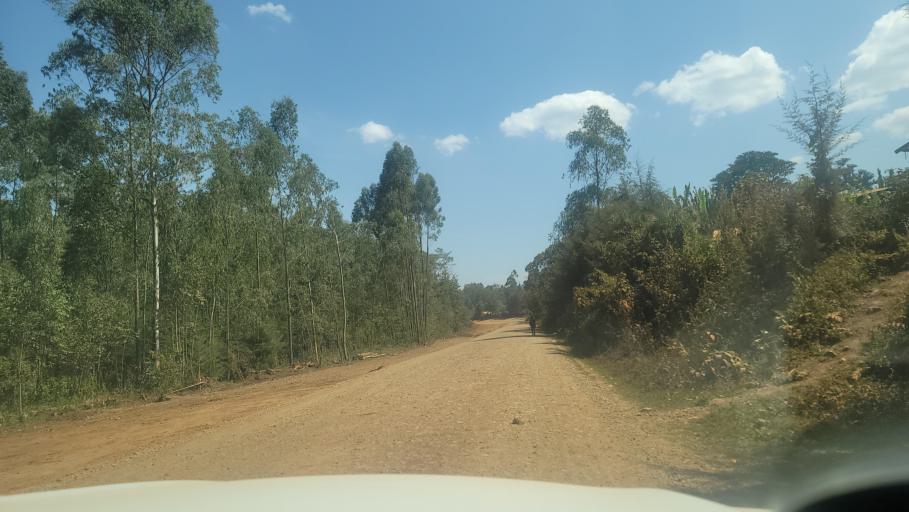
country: ET
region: Oromiya
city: Agaro
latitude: 7.7869
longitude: 36.4055
